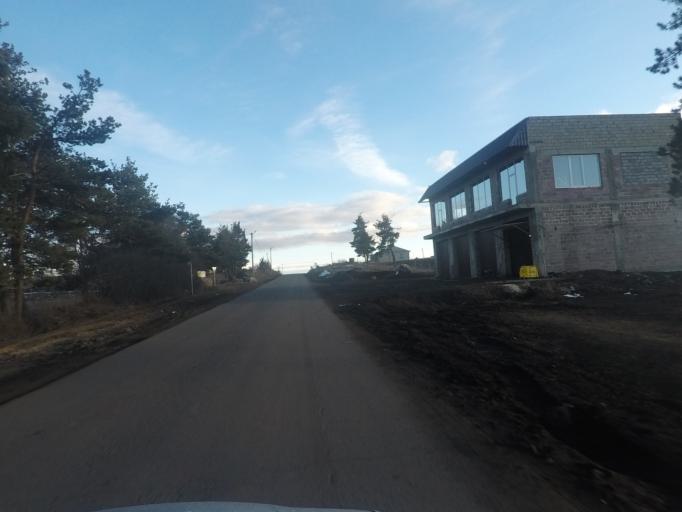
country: GE
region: Kvemo Kartli
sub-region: Tsalka
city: Tsalka
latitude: 41.6003
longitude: 44.0738
